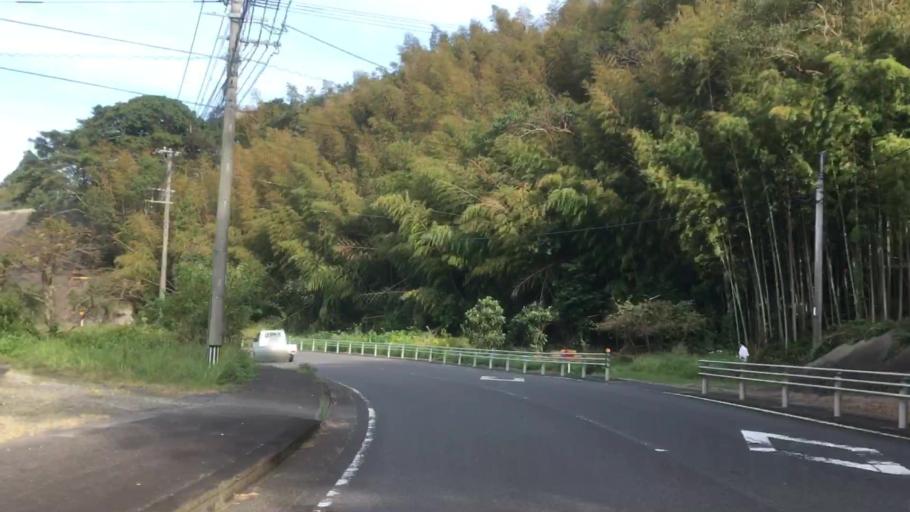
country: JP
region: Nagasaki
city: Sasebo
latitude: 33.0110
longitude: 129.6559
